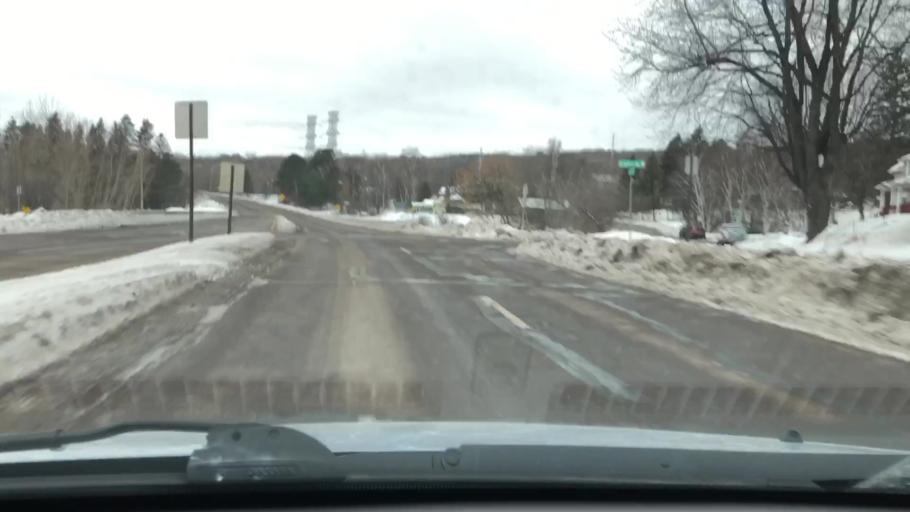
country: US
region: Minnesota
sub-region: Saint Louis County
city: Proctor
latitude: 46.7411
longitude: -92.1792
